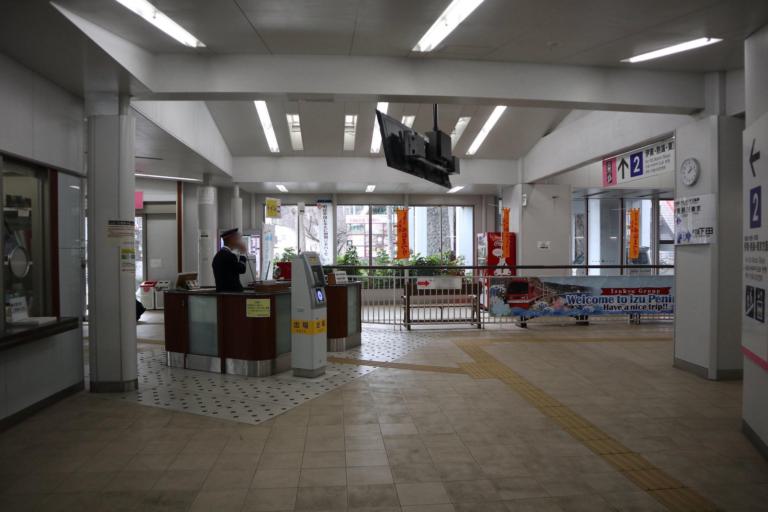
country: JP
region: Shizuoka
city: Shimoda
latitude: 34.7475
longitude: 138.9961
